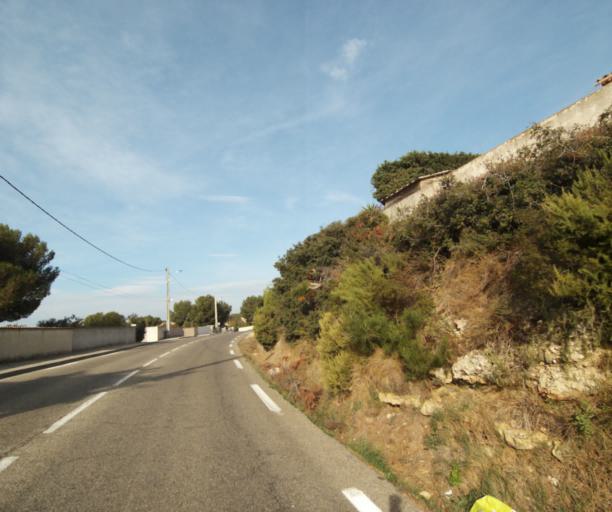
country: FR
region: Provence-Alpes-Cote d'Azur
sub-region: Departement des Bouches-du-Rhone
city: Carry-le-Rouet
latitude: 43.3314
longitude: 5.1661
